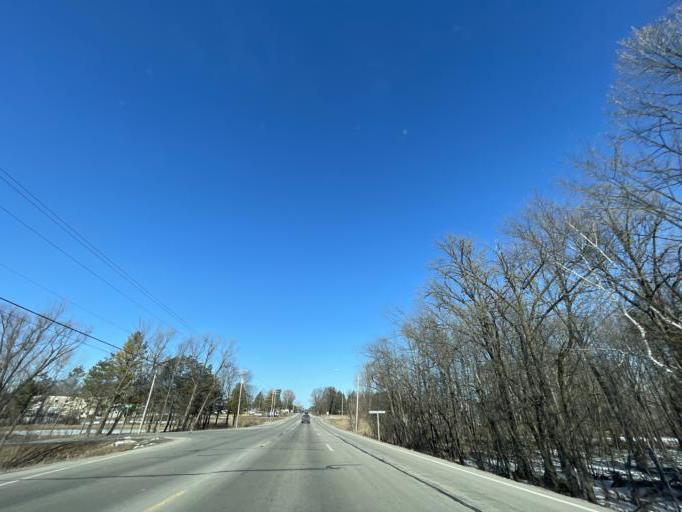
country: US
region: Wisconsin
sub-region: Brown County
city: Suamico
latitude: 44.6161
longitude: -88.0684
